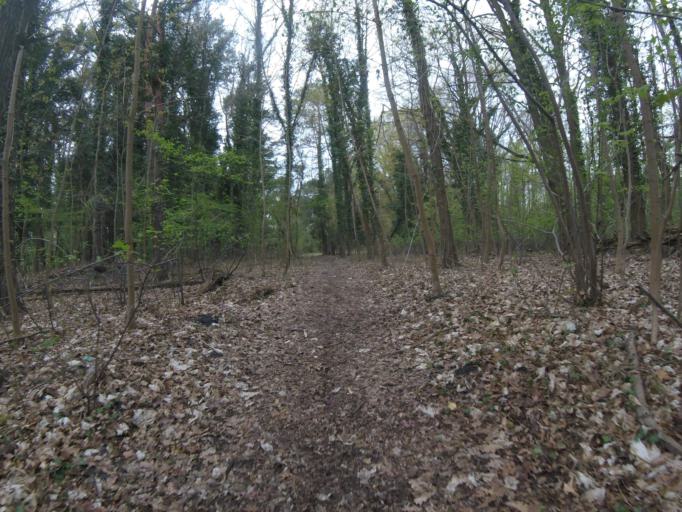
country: DE
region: Brandenburg
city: Bestensee
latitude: 52.2296
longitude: 13.6609
